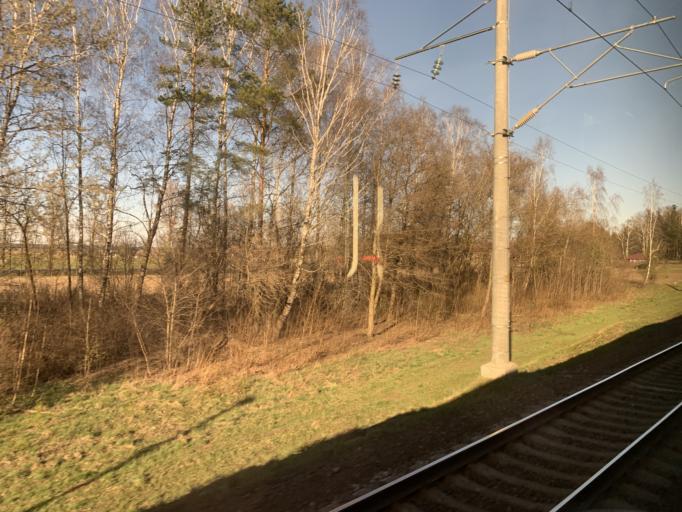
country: BY
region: Minsk
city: Maladzyechna
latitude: 54.2848
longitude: 26.9478
